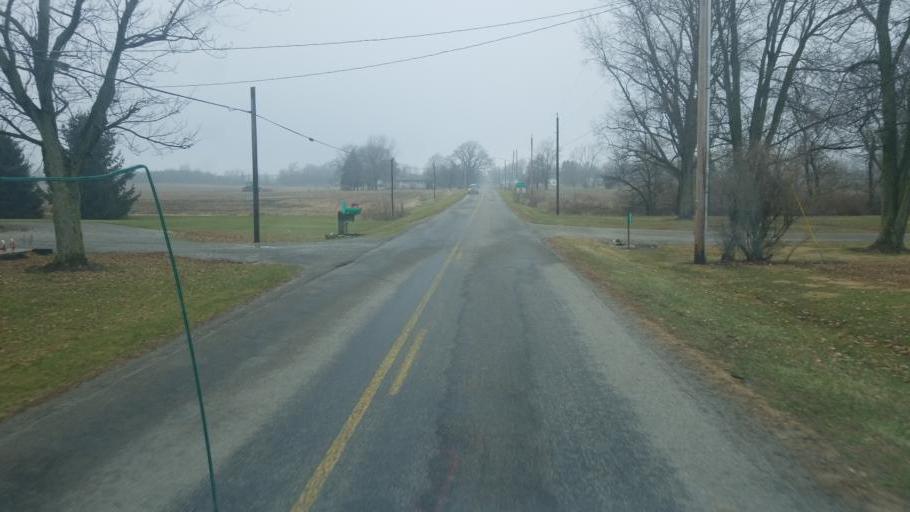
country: US
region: Ohio
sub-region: Hardin County
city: Kenton
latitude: 40.5268
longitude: -83.5244
